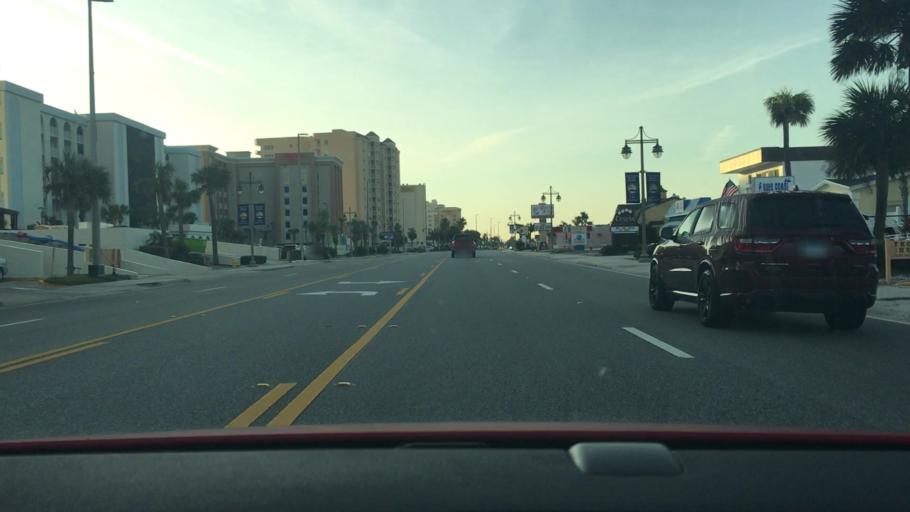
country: US
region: Florida
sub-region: Volusia County
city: Daytona Beach Shores
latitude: 29.1643
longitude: -80.9762
